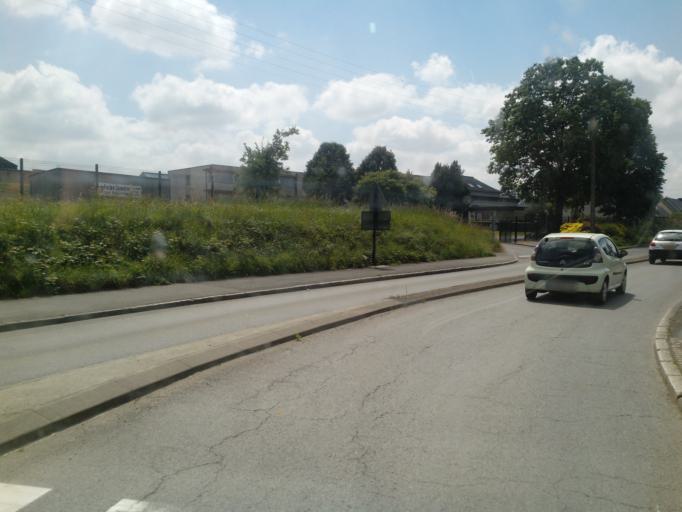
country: FR
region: Brittany
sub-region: Departement d'Ille-et-Vilaine
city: Lecousse
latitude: 48.3669
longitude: -1.2089
